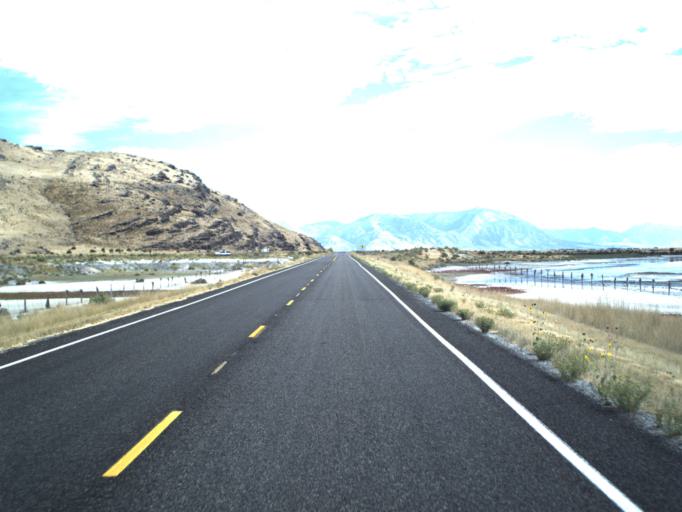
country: US
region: Utah
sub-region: Box Elder County
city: Tremonton
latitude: 41.5844
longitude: -112.2620
